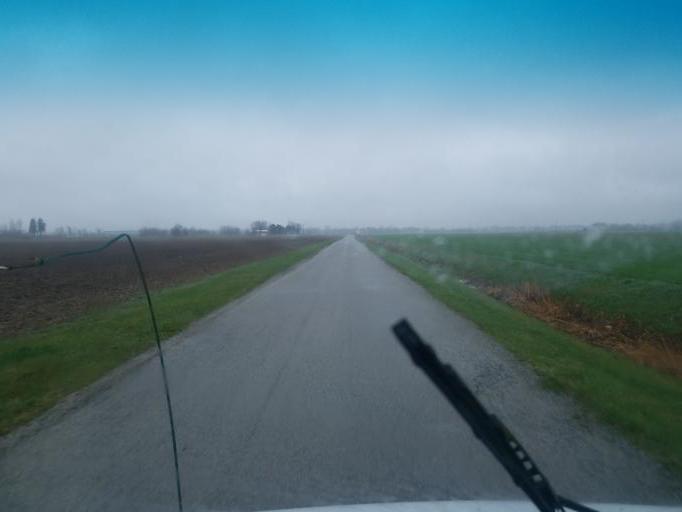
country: US
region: Ohio
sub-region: Wood County
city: North Baltimore
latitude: 41.2582
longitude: -83.6314
